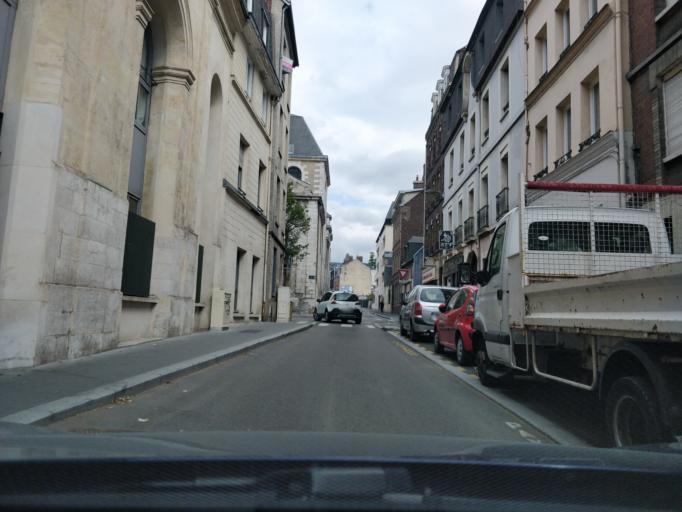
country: FR
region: Haute-Normandie
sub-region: Departement de la Seine-Maritime
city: Rouen
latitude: 49.4478
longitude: 1.0954
